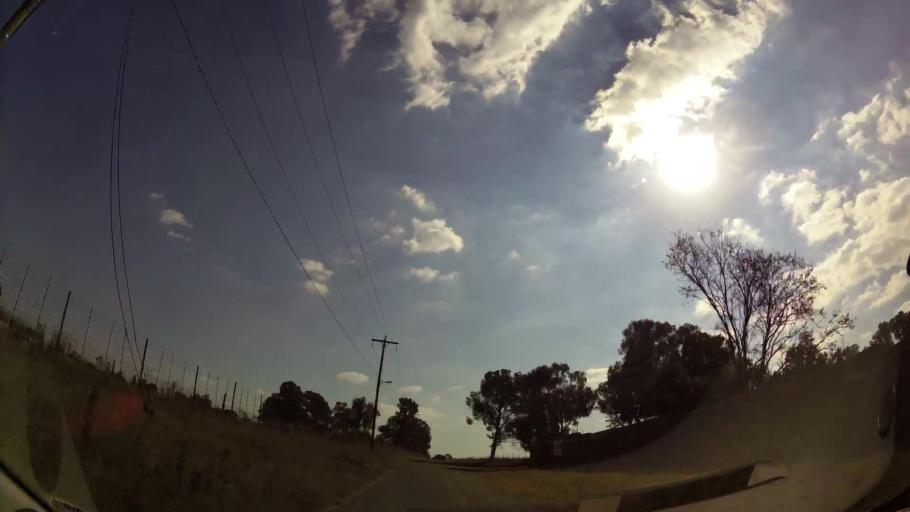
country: ZA
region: Gauteng
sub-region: Ekurhuleni Metropolitan Municipality
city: Benoni
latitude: -26.0877
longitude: 28.3567
